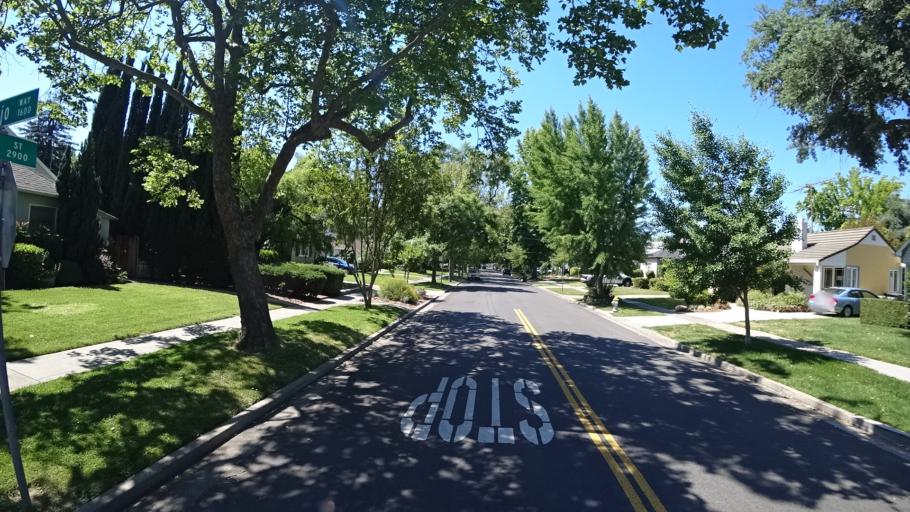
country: US
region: California
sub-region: Sacramento County
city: Sacramento
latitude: 38.5522
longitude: -121.4942
